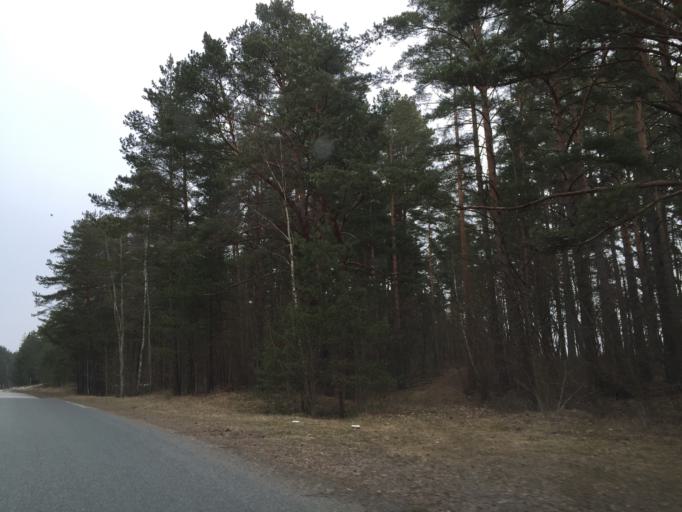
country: LV
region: Salacgrivas
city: Ainazi
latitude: 58.0201
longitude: 24.4540
